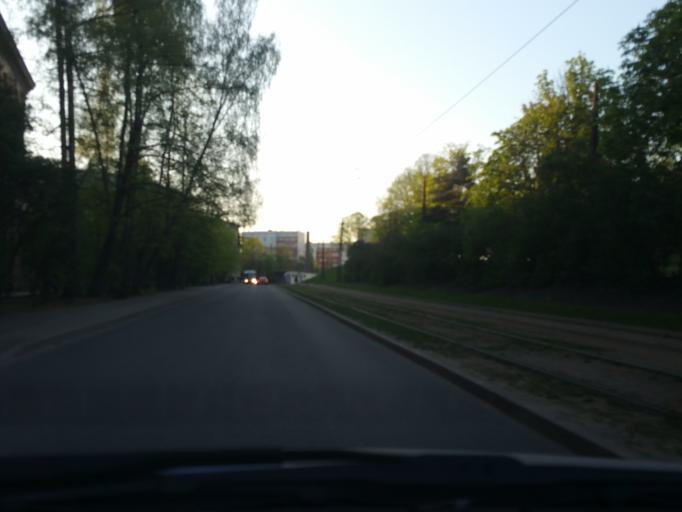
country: LV
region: Riga
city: Riga
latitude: 56.9961
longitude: 24.1250
